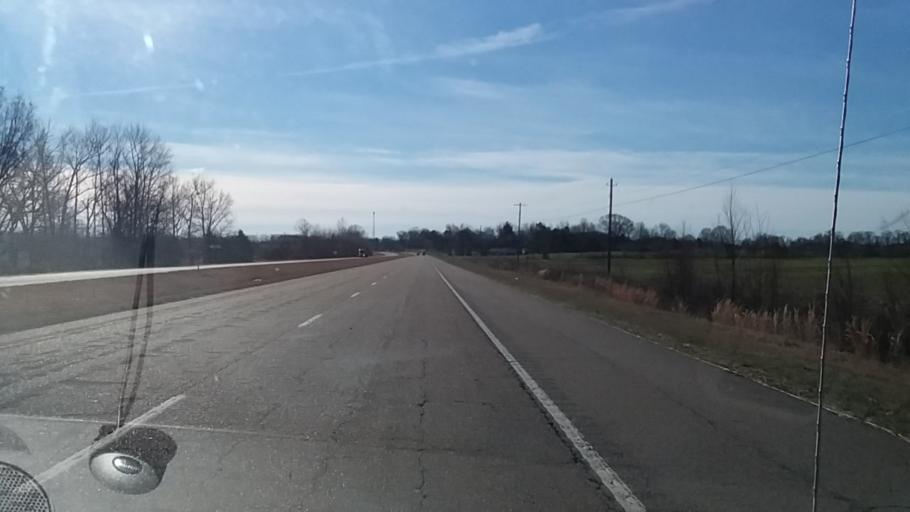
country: US
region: Tennessee
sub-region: Lauderdale County
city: Halls
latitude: 35.9224
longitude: -89.2781
